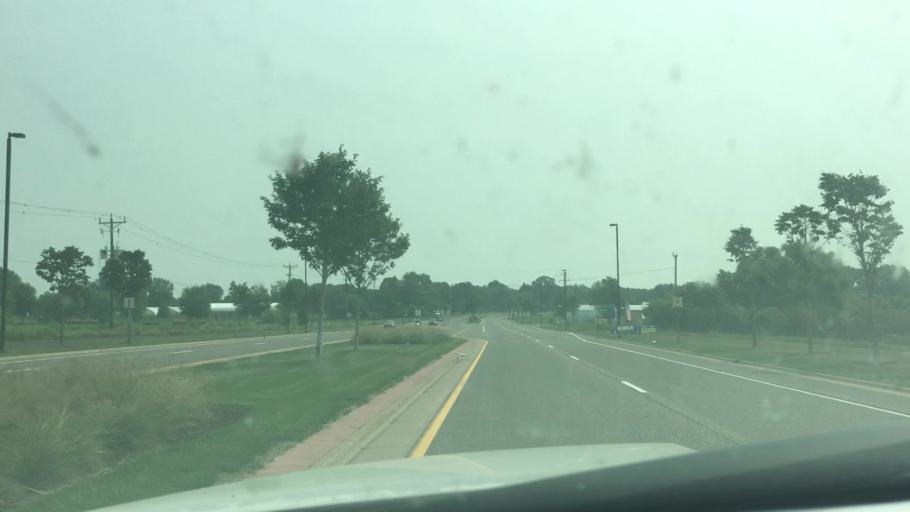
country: US
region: Minnesota
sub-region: Washington County
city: Hugo
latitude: 45.1631
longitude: -93.0107
